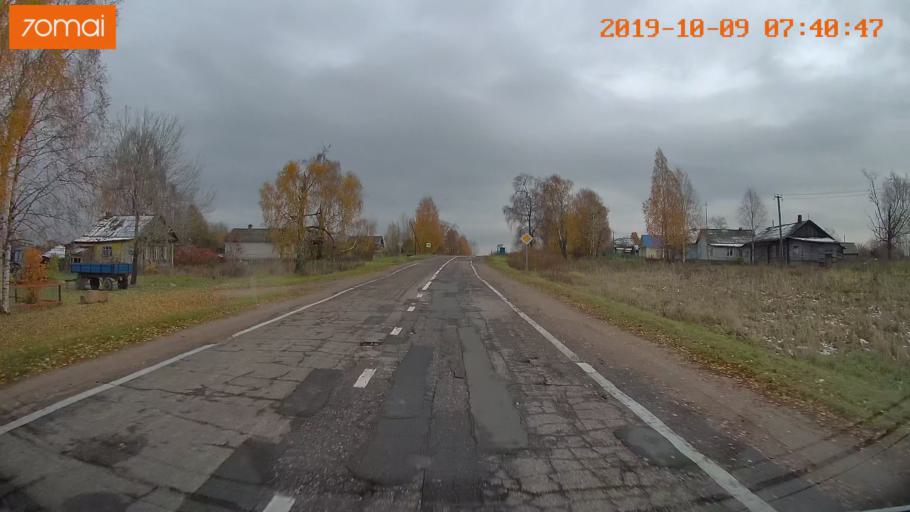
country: RU
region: Jaroslavl
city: Kukoboy
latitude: 58.6360
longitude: 39.6978
